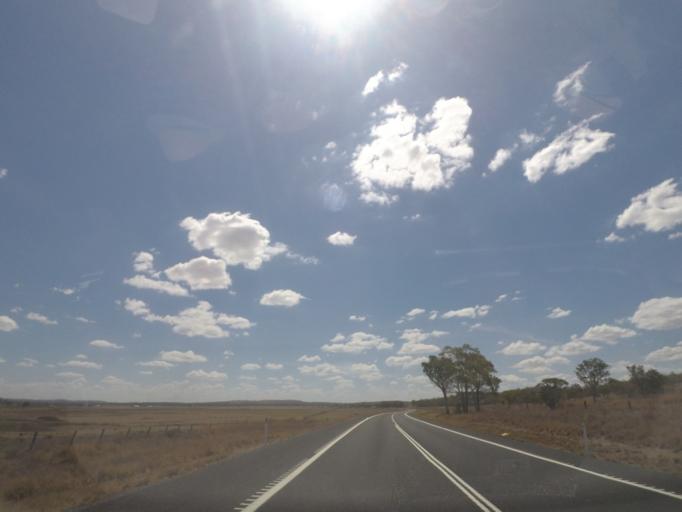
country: AU
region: Queensland
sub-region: Southern Downs
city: Warwick
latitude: -28.1807
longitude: 151.7892
